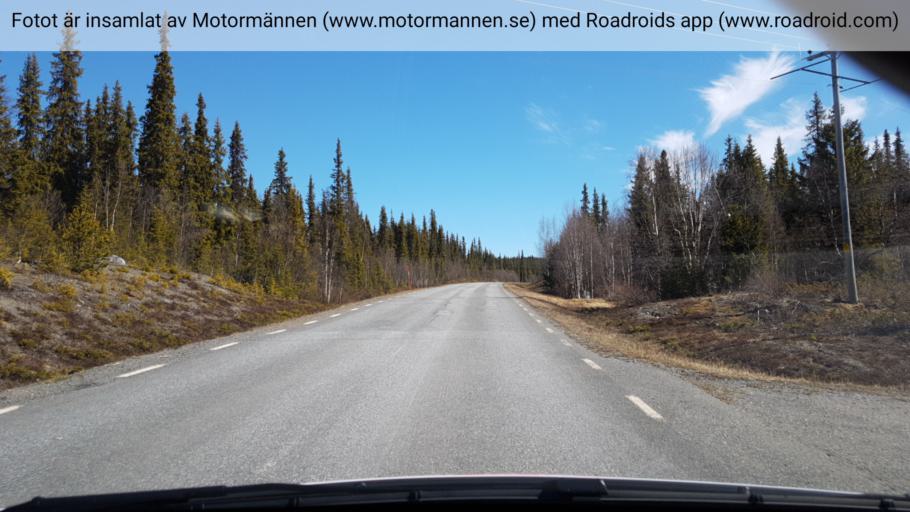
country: SE
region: Vaesterbotten
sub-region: Vilhelmina Kommun
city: Sjoberg
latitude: 65.0313
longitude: 15.8771
